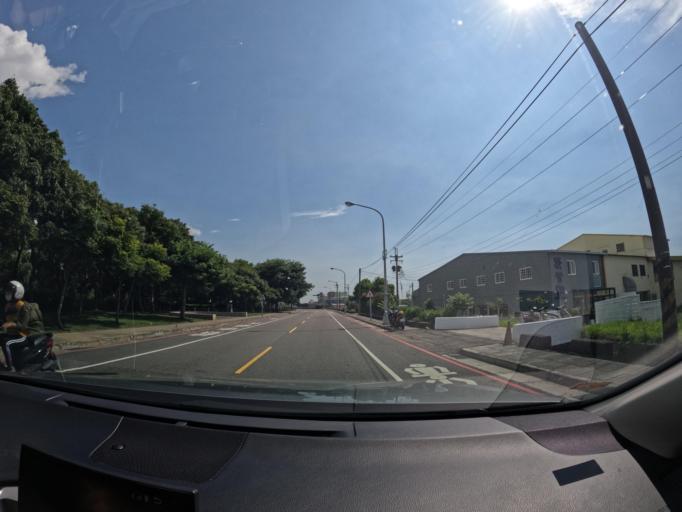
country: TW
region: Taiwan
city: Fengyuan
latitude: 24.3174
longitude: 120.7190
